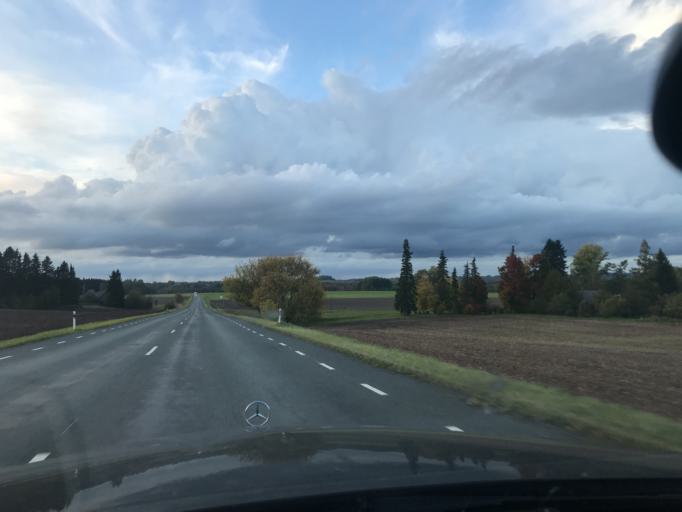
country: EE
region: Vorumaa
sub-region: Antsla vald
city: Vana-Antsla
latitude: 57.9186
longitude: 26.3503
